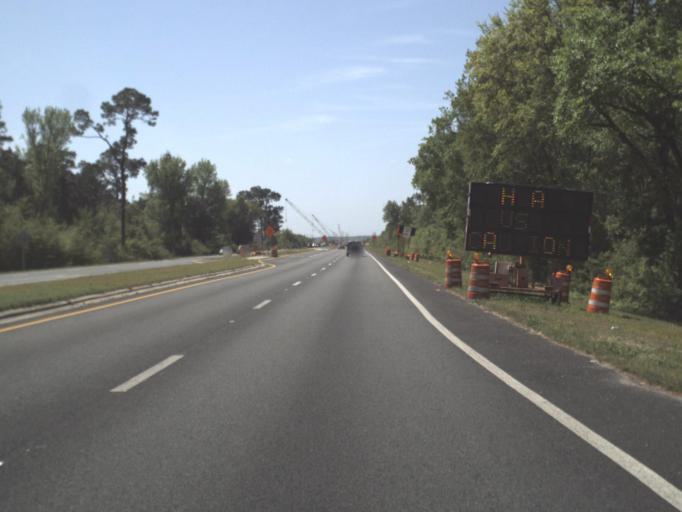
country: US
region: Florida
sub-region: Santa Rosa County
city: Pace
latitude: 30.5892
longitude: -87.1763
